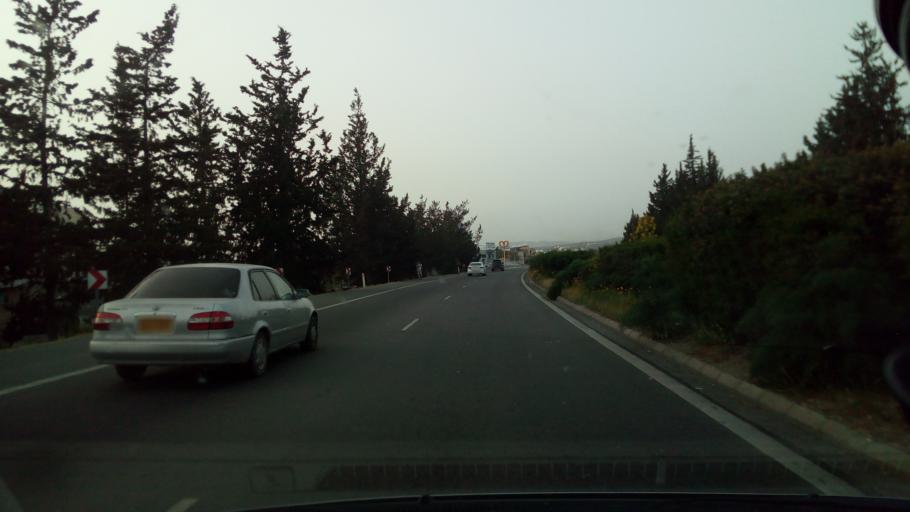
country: CY
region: Limassol
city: Pano Polemidia
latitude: 34.6829
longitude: 33.0082
